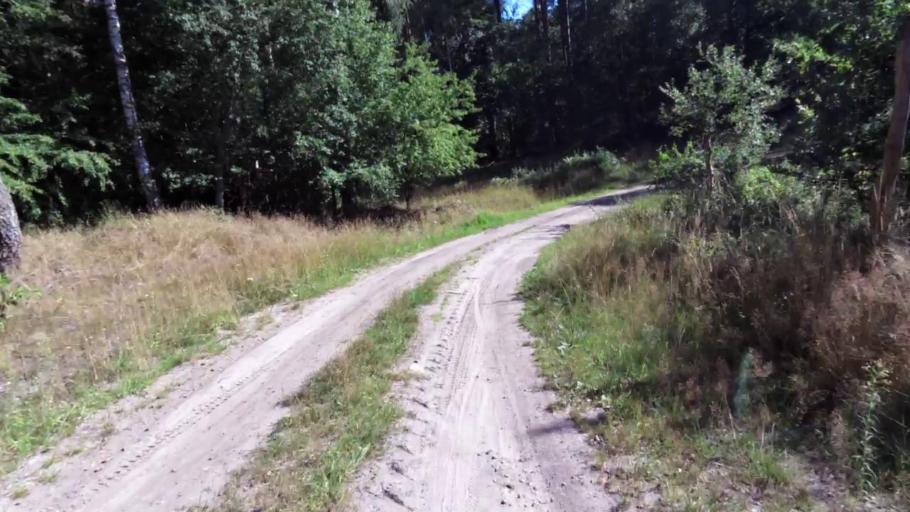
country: PL
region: West Pomeranian Voivodeship
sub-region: Powiat szczecinecki
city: Borne Sulinowo
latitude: 53.6040
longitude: 16.6085
